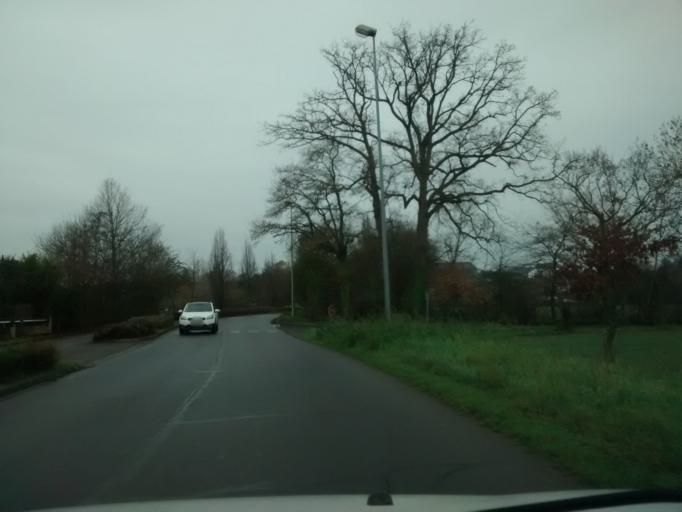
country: FR
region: Brittany
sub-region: Departement d'Ille-et-Vilaine
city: Acigne
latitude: 48.1285
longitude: -1.5330
